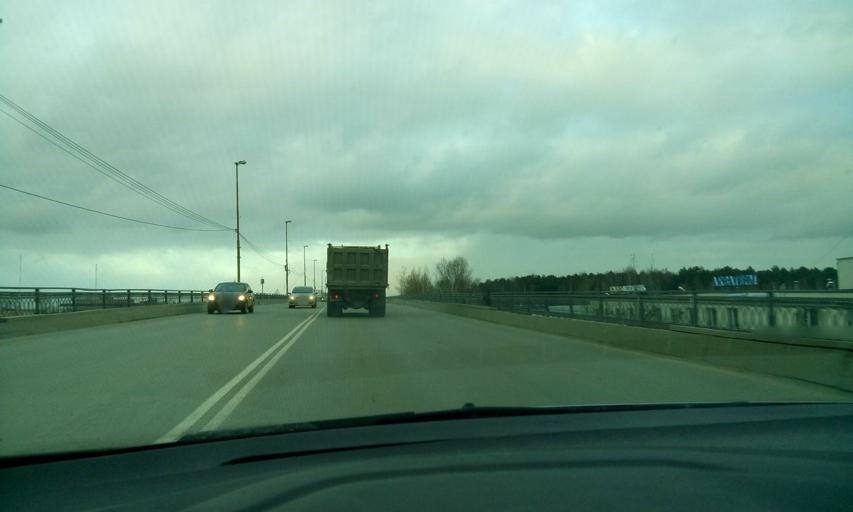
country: RU
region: Sverdlovsk
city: Yekaterinburg
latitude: 56.8654
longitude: 60.6707
